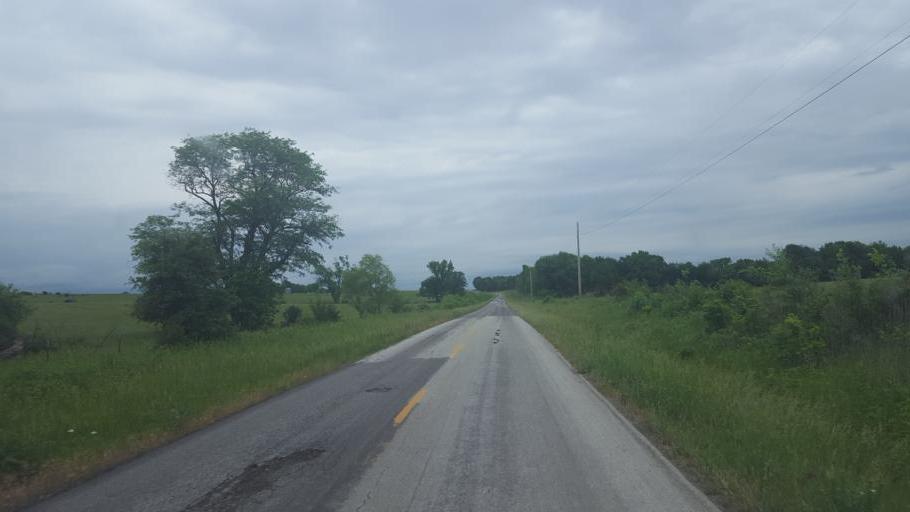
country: US
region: Missouri
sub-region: Moniteau County
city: California
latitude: 38.7759
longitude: -92.6051
